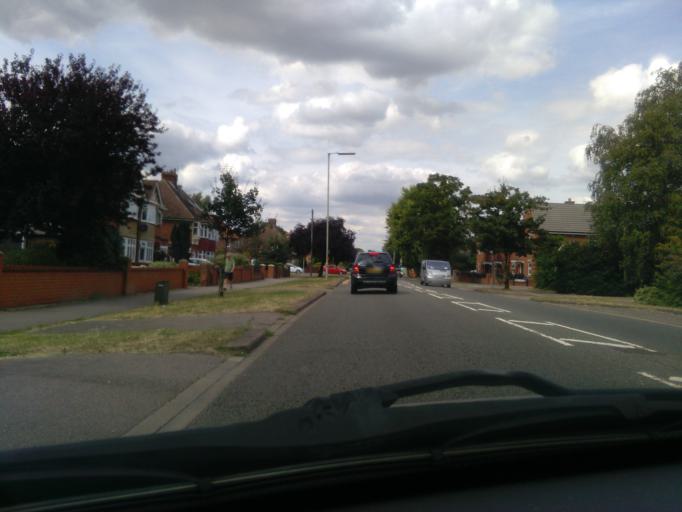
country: GB
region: England
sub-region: Bedford
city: Bedford
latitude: 52.1374
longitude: -0.4446
